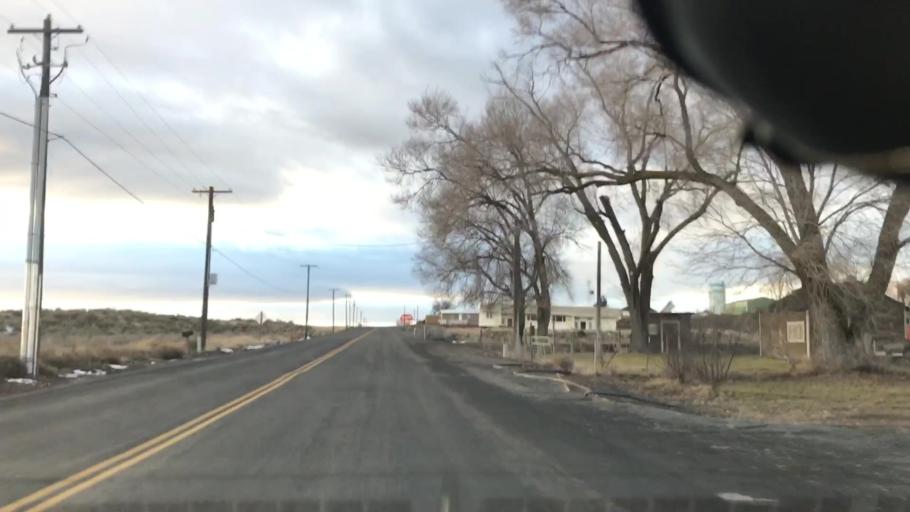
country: US
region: Washington
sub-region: Grant County
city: Moses Lake
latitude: 47.1016
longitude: -119.2367
